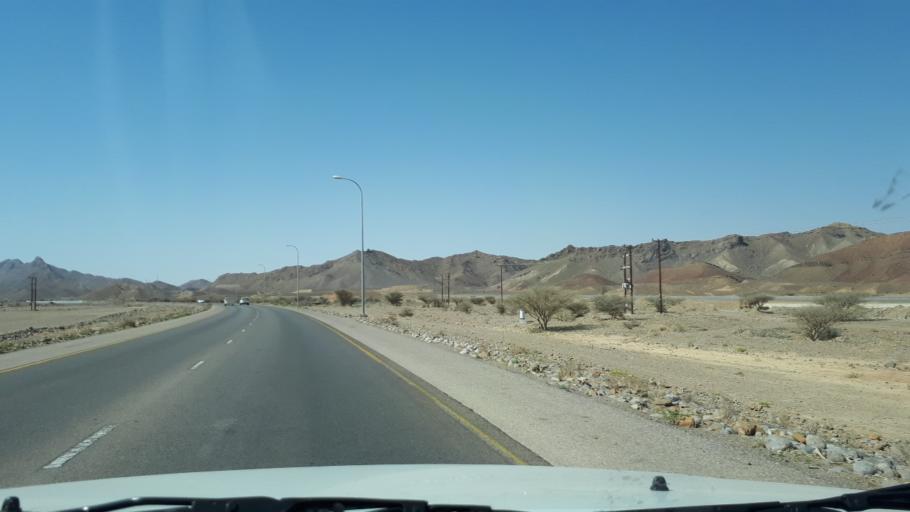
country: OM
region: Ash Sharqiyah
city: Sur
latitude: 22.3643
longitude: 59.3129
